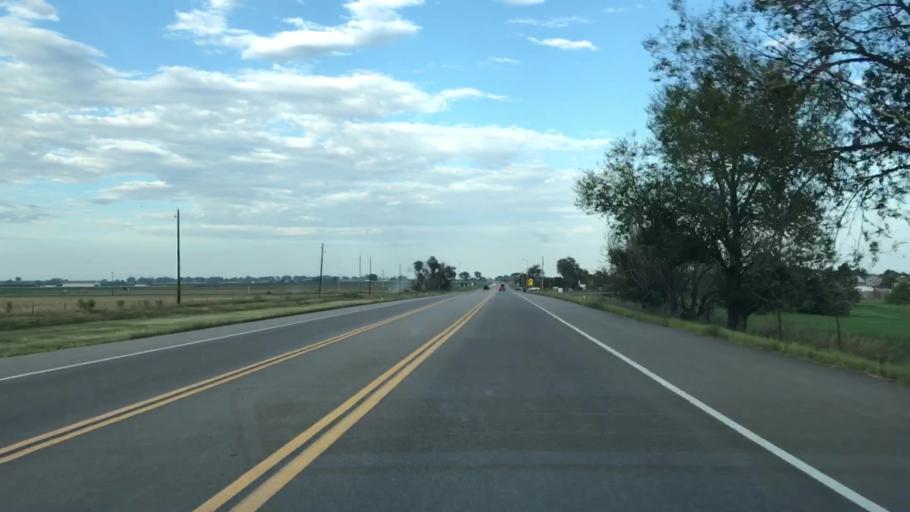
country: US
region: Colorado
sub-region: Boulder County
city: Longmont
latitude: 40.2031
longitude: -105.0879
